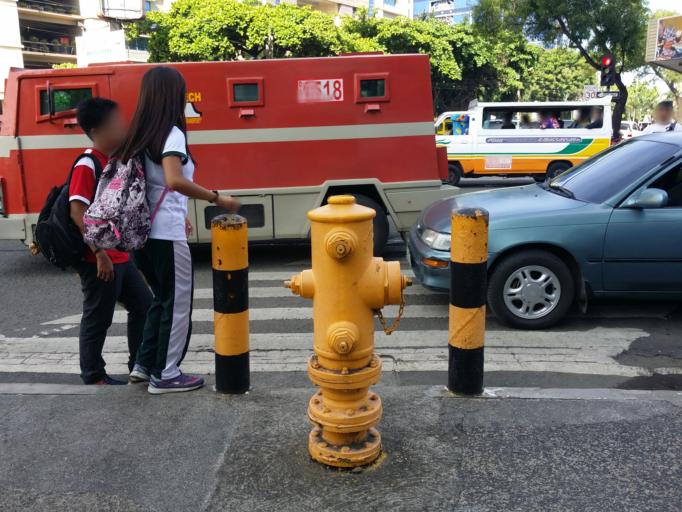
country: PH
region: Davao
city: Davao
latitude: 7.0719
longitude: 125.6119
